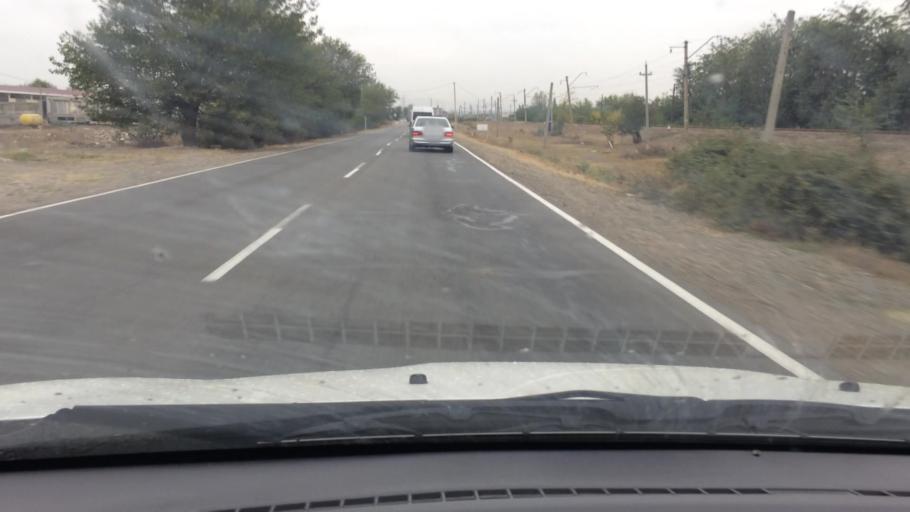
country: GE
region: Kvemo Kartli
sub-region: Marneuli
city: Marneuli
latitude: 41.4562
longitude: 44.8116
